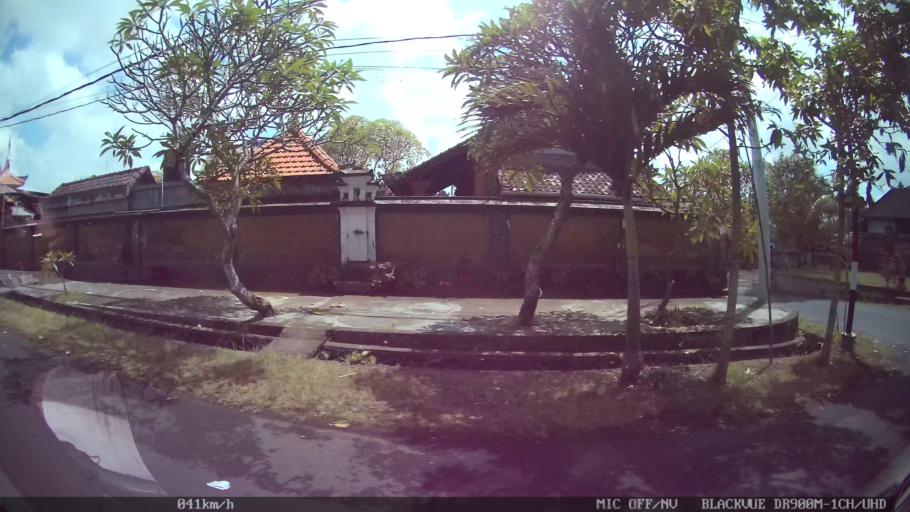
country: ID
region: Bali
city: Banjar Pasekan
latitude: -8.5916
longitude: 115.2863
